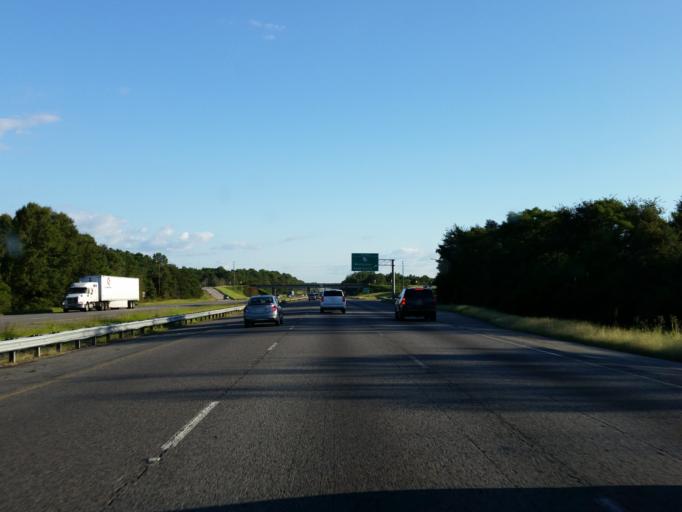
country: US
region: Georgia
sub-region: Dooly County
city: Unadilla
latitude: 32.3405
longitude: -83.7684
